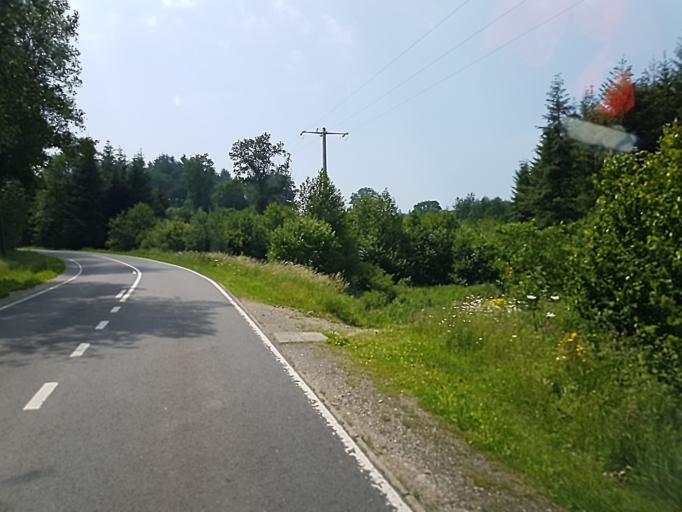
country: BE
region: Wallonia
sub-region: Province de Liege
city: Lierneux
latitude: 50.3255
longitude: 5.7462
